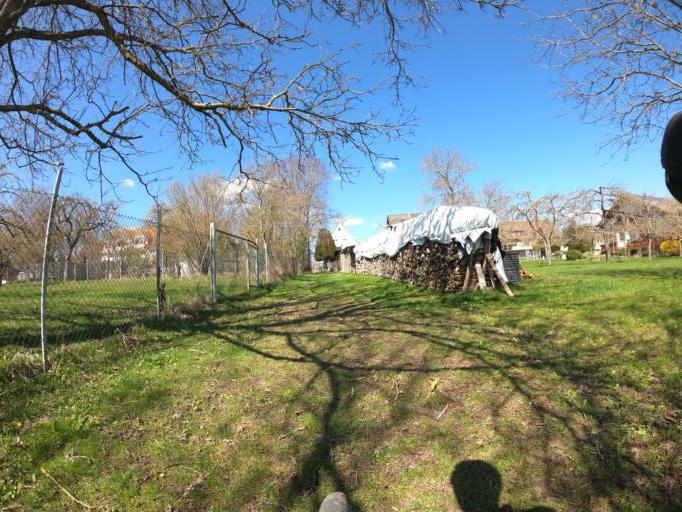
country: DE
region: Baden-Wuerttemberg
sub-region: Karlsruhe Region
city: Horb am Neckar
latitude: 48.4340
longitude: 8.7086
